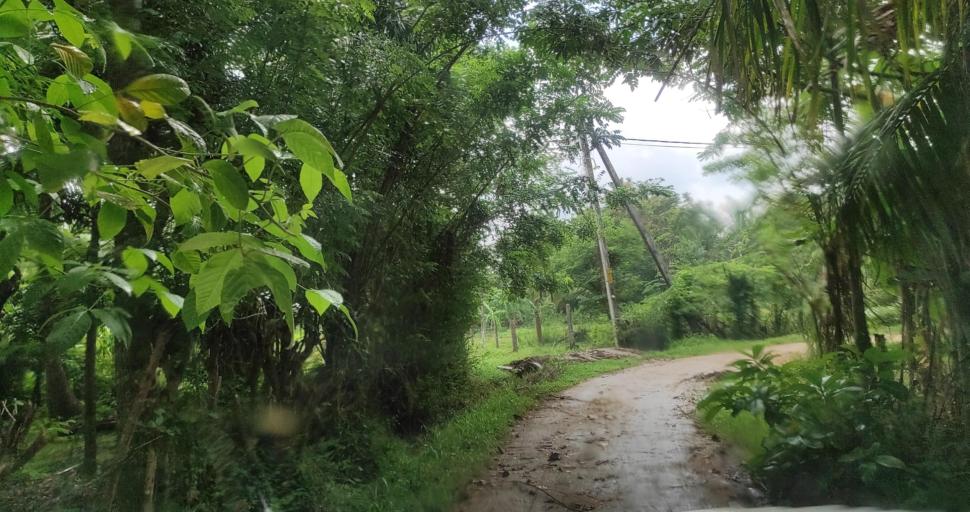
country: LK
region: Eastern Province
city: Trincomalee
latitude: 8.3718
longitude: 81.0158
